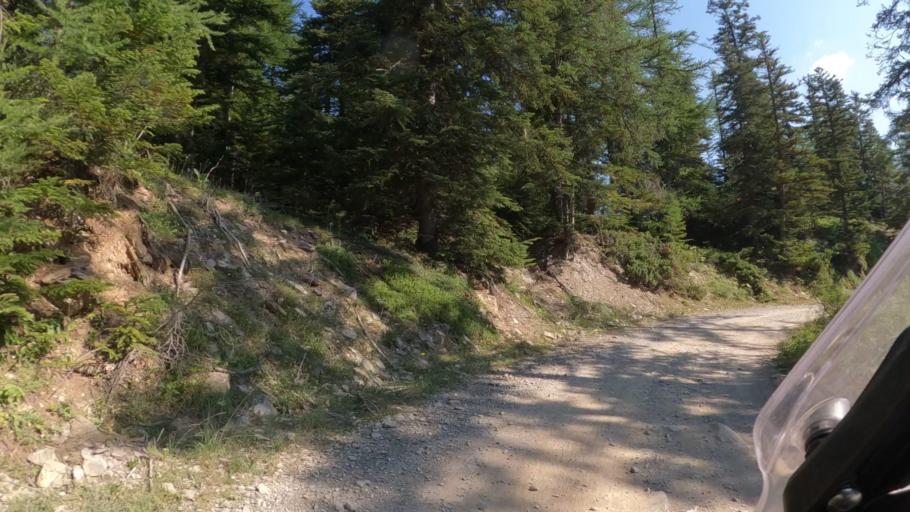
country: FR
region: Provence-Alpes-Cote d'Azur
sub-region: Departement des Hautes-Alpes
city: Embrun
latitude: 44.5932
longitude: 6.5731
